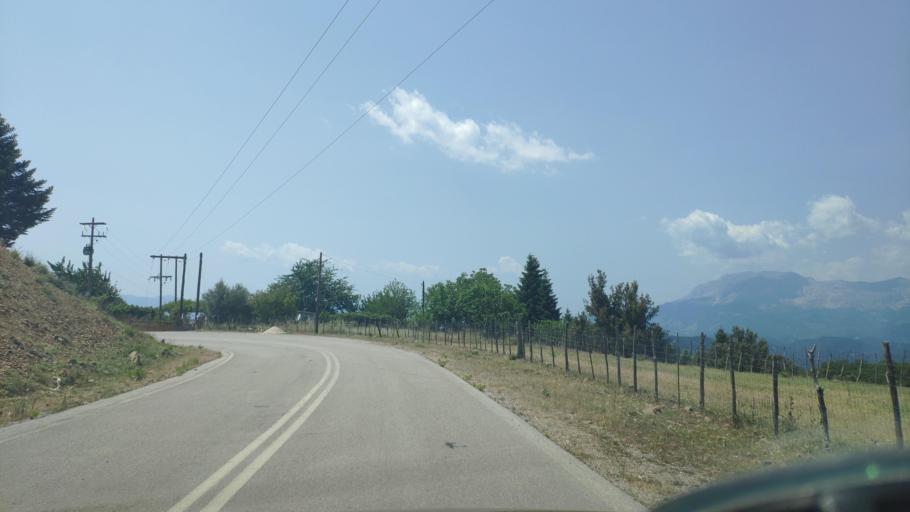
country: GR
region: Epirus
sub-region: Nomos Artas
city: Ano Kalentini
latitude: 39.2391
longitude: 21.2173
